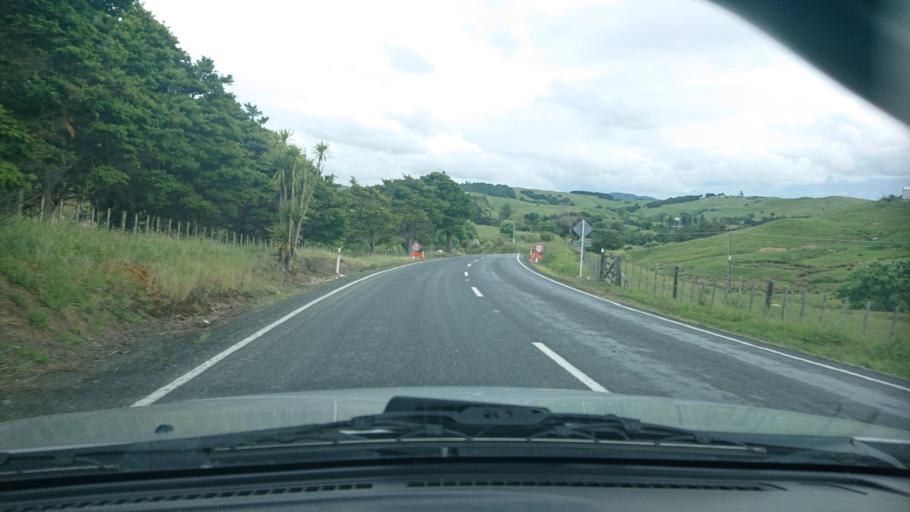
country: NZ
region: Auckland
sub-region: Auckland
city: Wellsford
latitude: -36.3709
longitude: 174.4539
